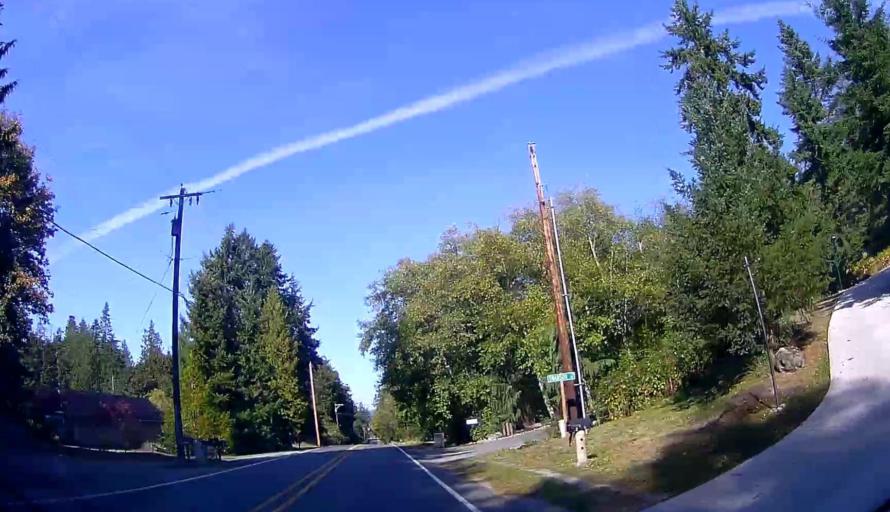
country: US
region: Washington
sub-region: Island County
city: Camano
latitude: 48.2346
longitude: -122.5209
